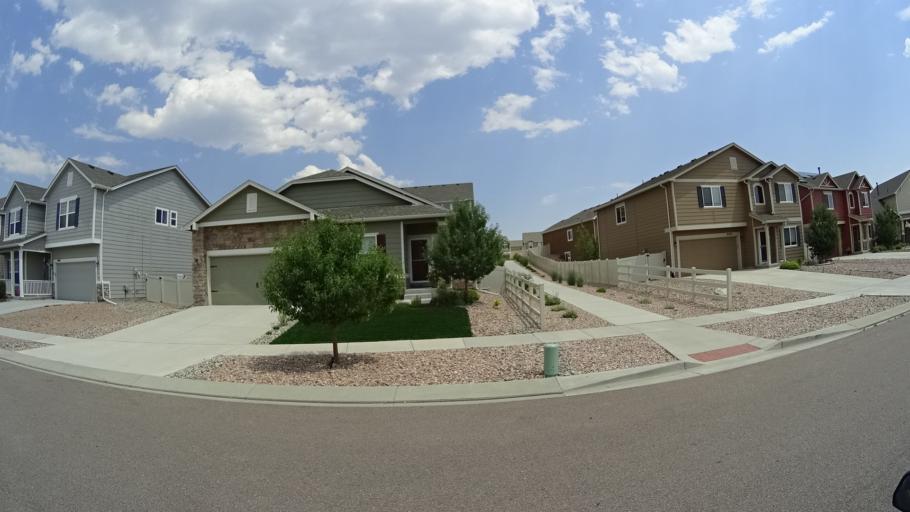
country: US
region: Colorado
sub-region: El Paso County
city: Black Forest
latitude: 38.9512
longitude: -104.6937
